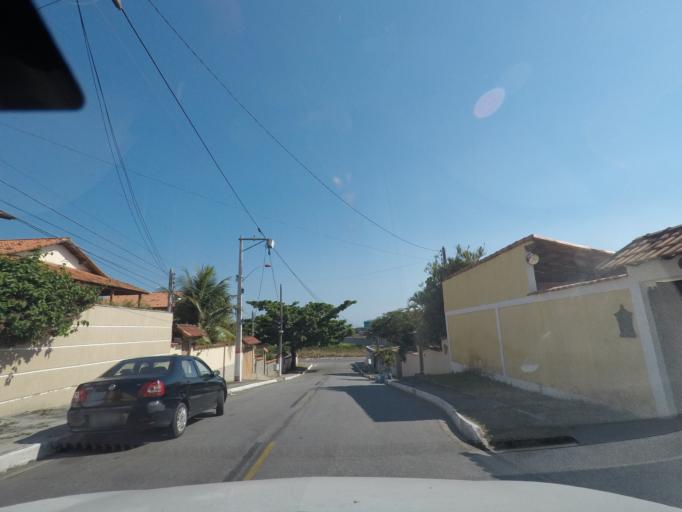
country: BR
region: Rio de Janeiro
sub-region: Niteroi
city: Niteroi
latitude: -22.9667
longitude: -42.9738
